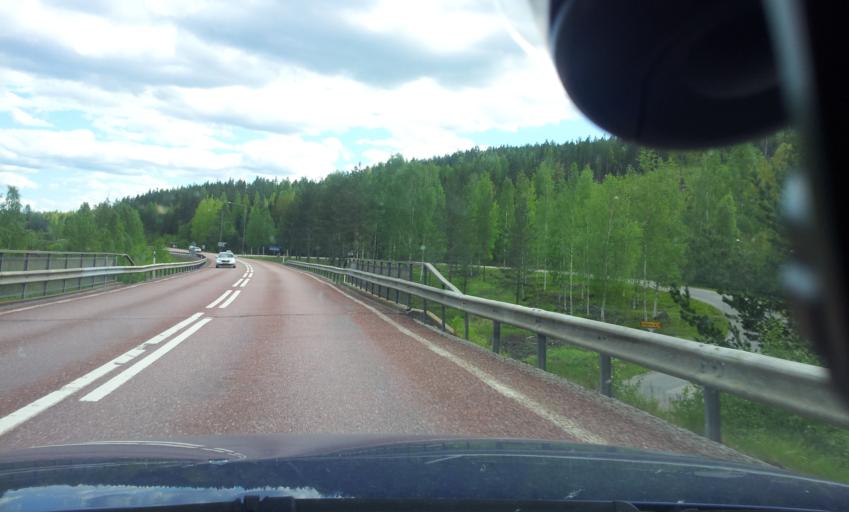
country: SE
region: Gaevleborg
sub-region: Bollnas Kommun
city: Arbra
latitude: 61.5967
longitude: 16.2969
